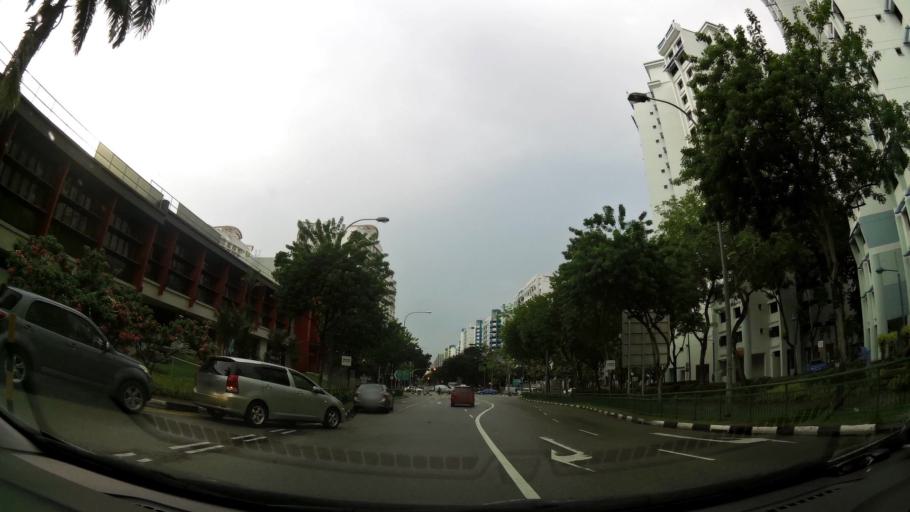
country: MY
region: Johor
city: Kampung Pasir Gudang Baru
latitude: 1.3859
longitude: 103.9025
